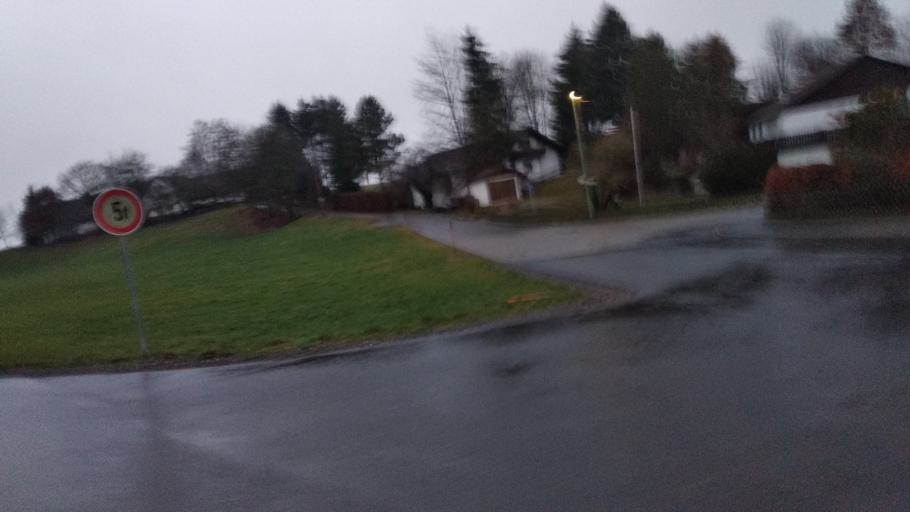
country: DE
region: Bavaria
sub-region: Swabia
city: Lautrach
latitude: 47.8862
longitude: 10.1350
